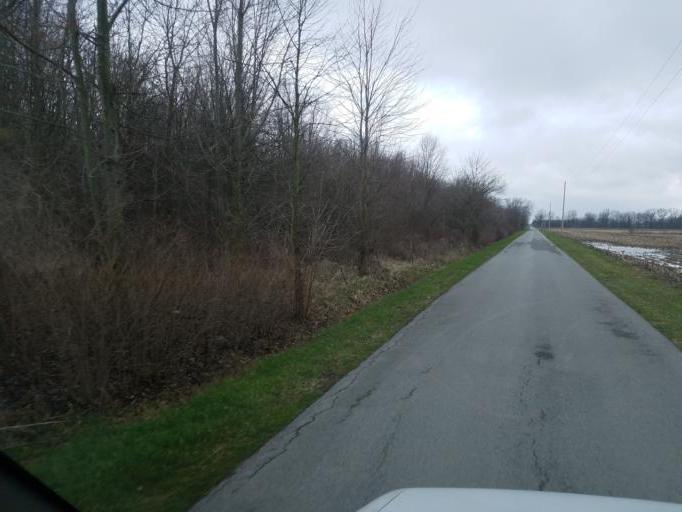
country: US
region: Ohio
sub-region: Wyandot County
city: Upper Sandusky
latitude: 40.6874
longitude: -83.3382
